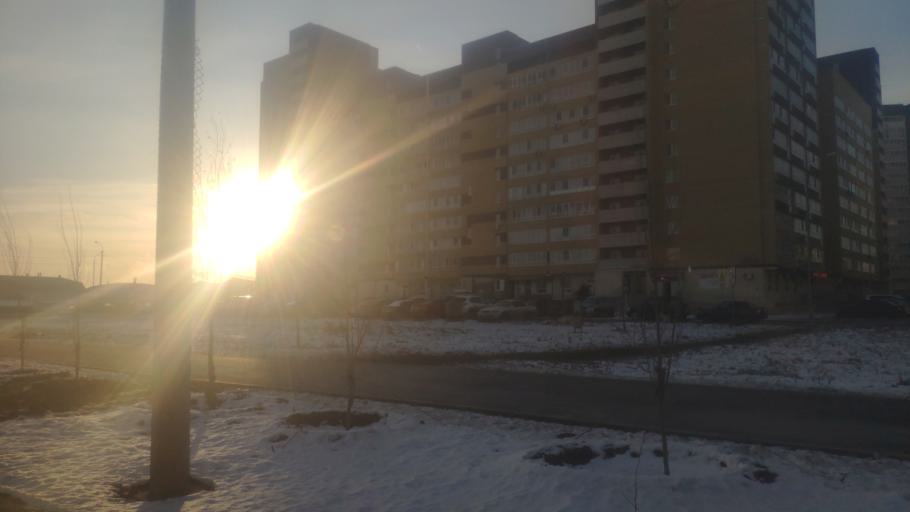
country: RU
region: Tjumen
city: Tyumen
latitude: 57.1784
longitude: 65.5677
